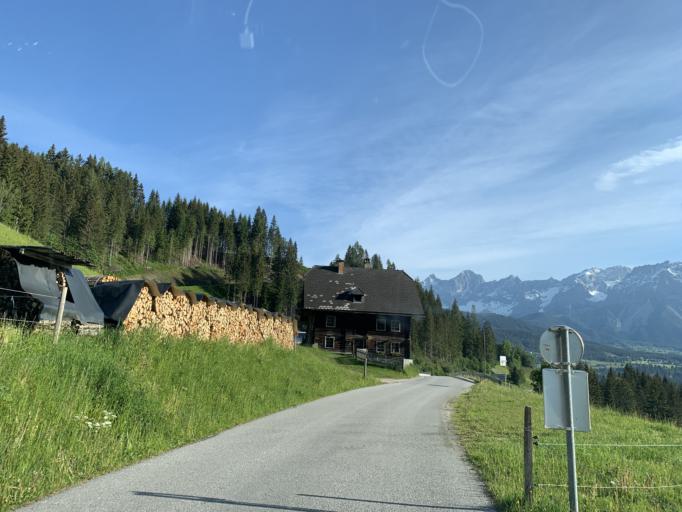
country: AT
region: Styria
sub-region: Politischer Bezirk Liezen
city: Schladming
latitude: 47.3735
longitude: 13.6141
